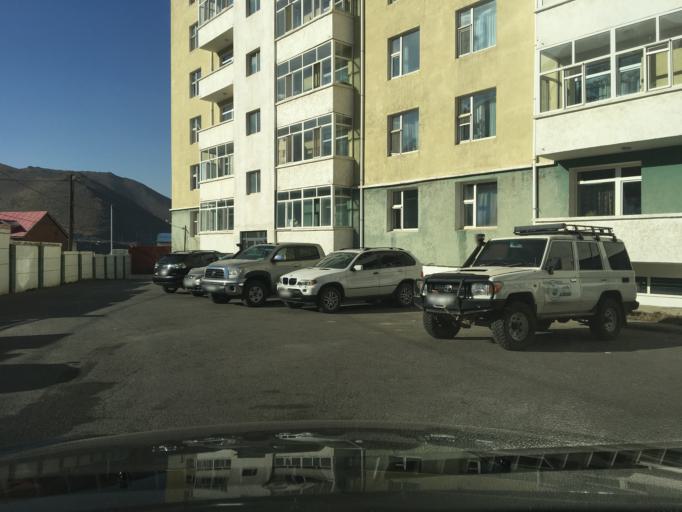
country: MN
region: Ulaanbaatar
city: Ulaanbaatar
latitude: 47.8872
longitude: 106.9030
